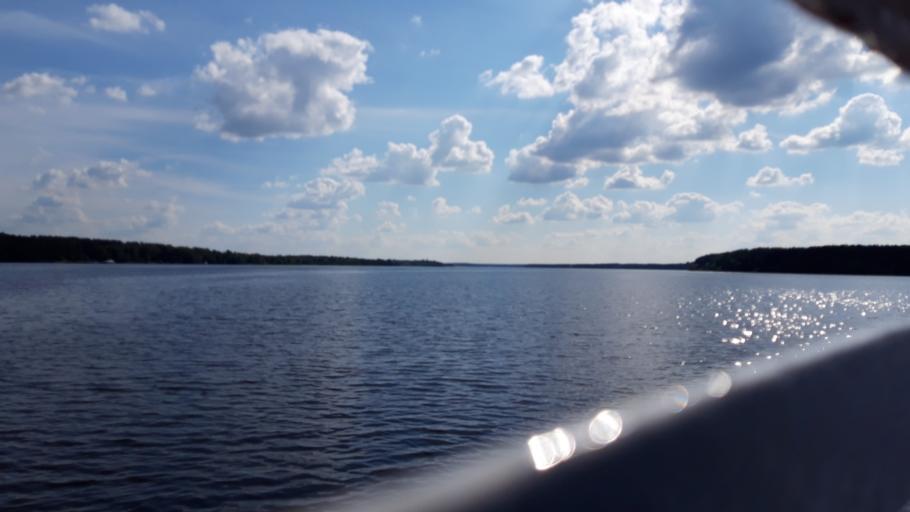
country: RU
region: Tverskaya
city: Konakovo
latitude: 56.6618
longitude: 36.6463
